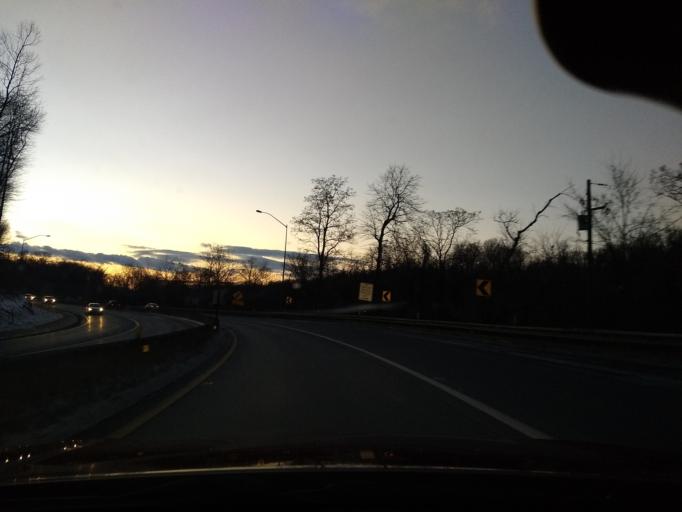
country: US
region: Pennsylvania
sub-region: Northampton County
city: Easton
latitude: 40.6998
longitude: -75.2157
